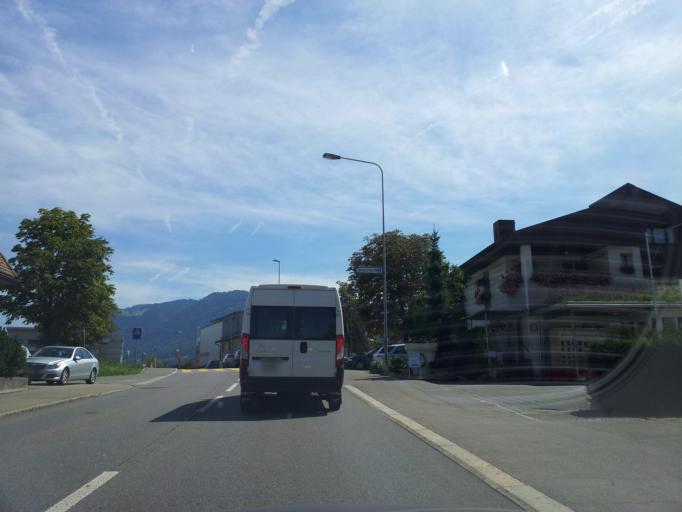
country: CH
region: Schwyz
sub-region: Bezirk March
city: Lachen
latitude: 47.1882
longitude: 8.8587
